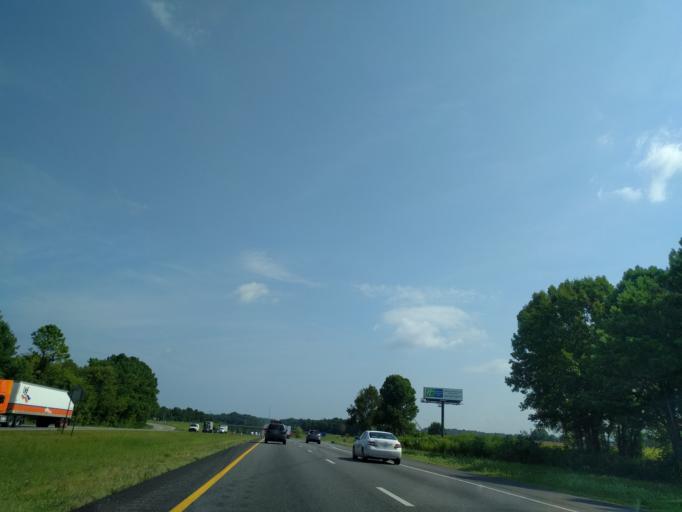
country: US
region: Tennessee
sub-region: Sumner County
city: White House
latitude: 36.5237
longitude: -86.6444
